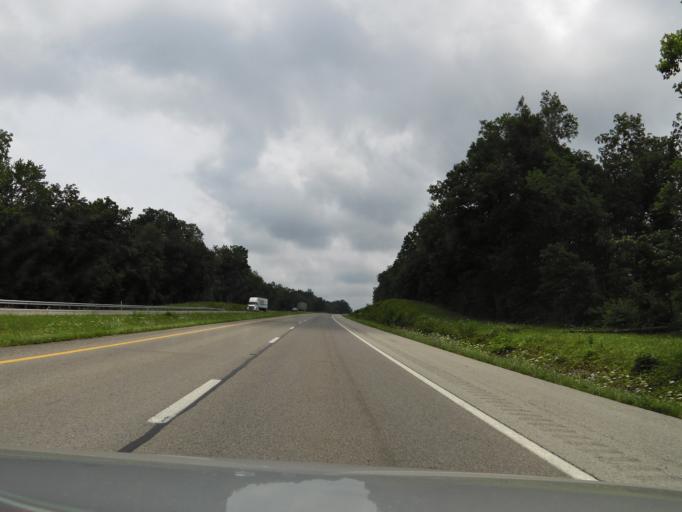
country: US
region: Kentucky
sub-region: Ohio County
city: Oak Grove
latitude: 37.3921
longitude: -86.7905
